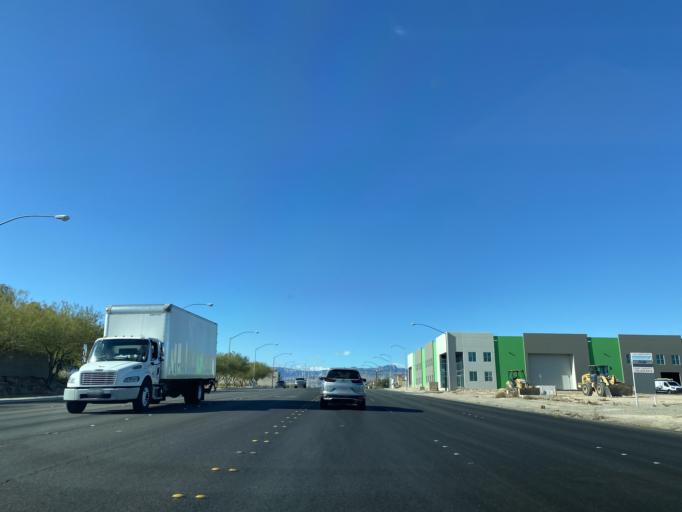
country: US
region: Nevada
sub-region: Clark County
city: Spring Valley
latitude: 36.0718
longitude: -115.2041
